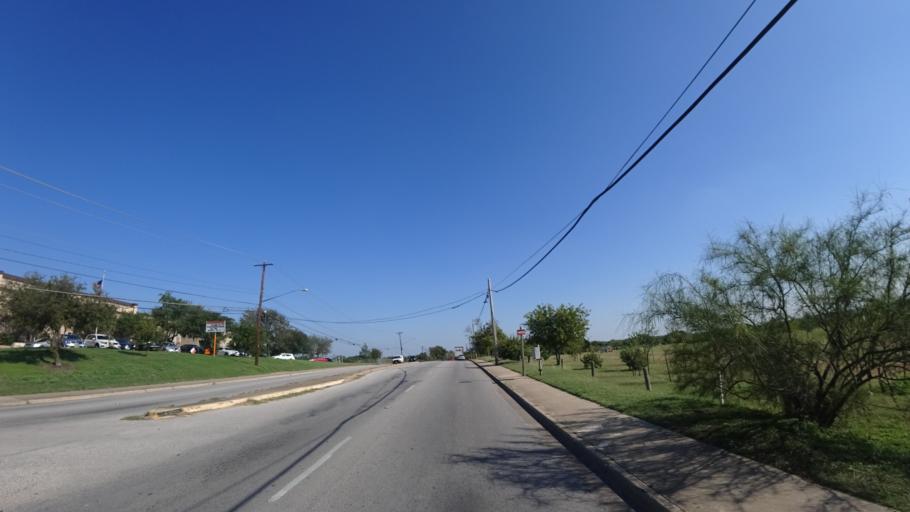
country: US
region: Texas
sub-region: Travis County
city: Wells Branch
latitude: 30.3537
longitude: -97.6810
